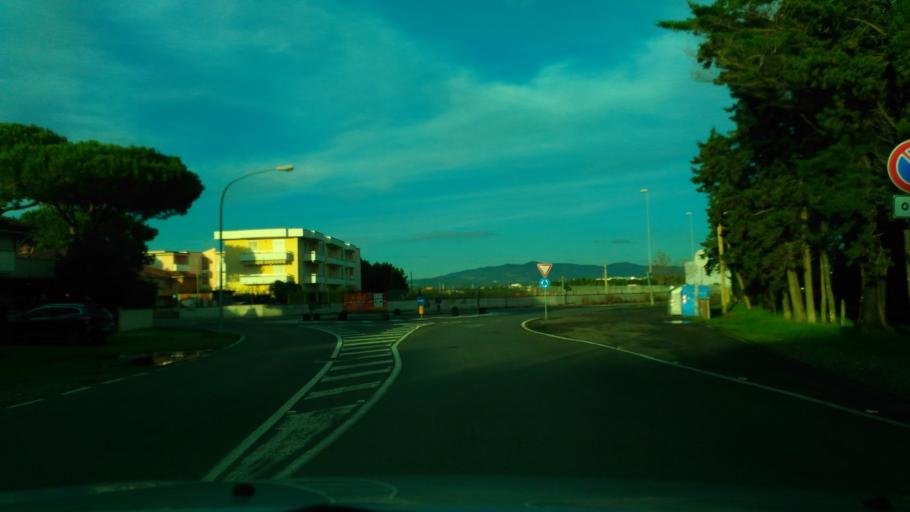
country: IT
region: Tuscany
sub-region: Provincia di Livorno
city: Cecina
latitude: 43.2951
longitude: 10.5027
